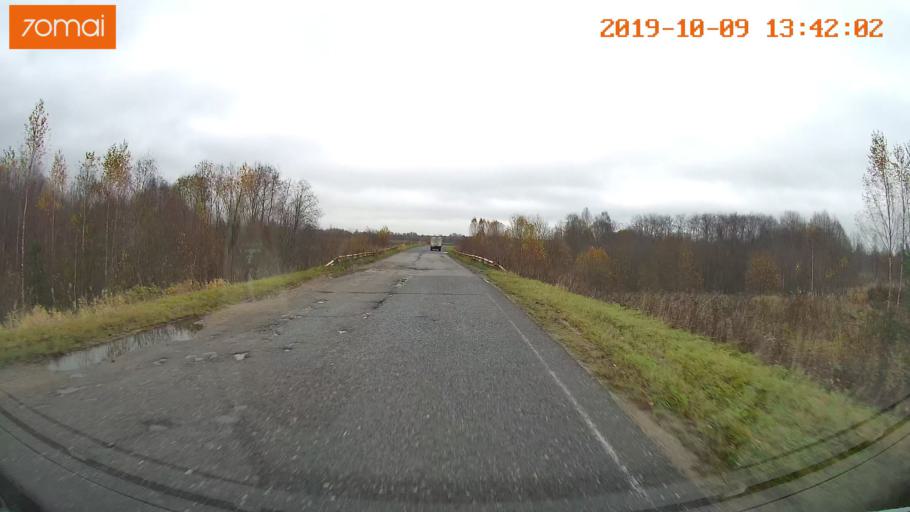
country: RU
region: Kostroma
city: Buy
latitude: 58.3536
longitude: 41.1816
